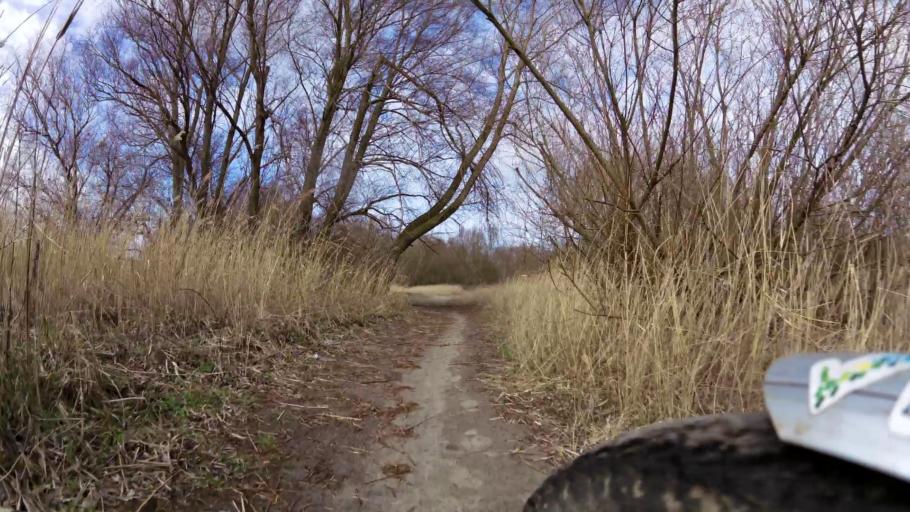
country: PL
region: West Pomeranian Voivodeship
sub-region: Powiat kamienski
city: Kamien Pomorski
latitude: 53.9789
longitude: 14.7703
